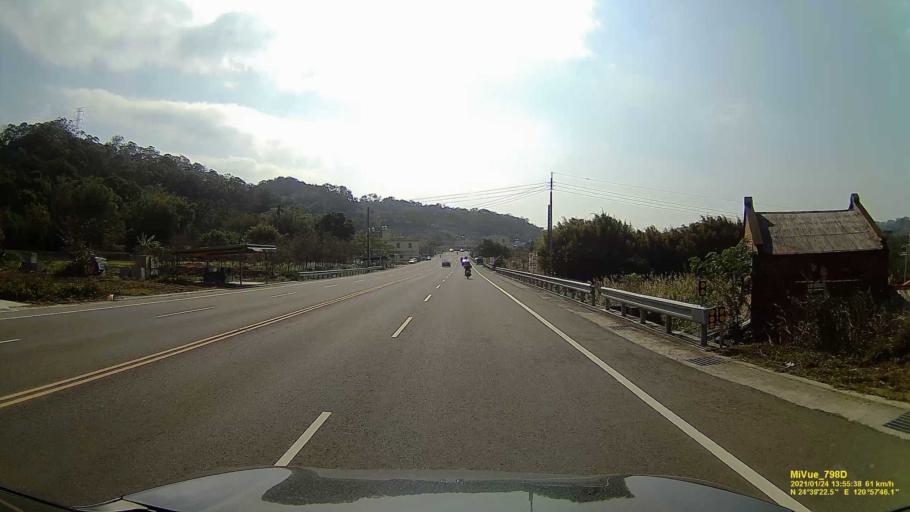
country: TW
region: Taiwan
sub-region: Hsinchu
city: Hsinchu
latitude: 24.6560
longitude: 120.9625
